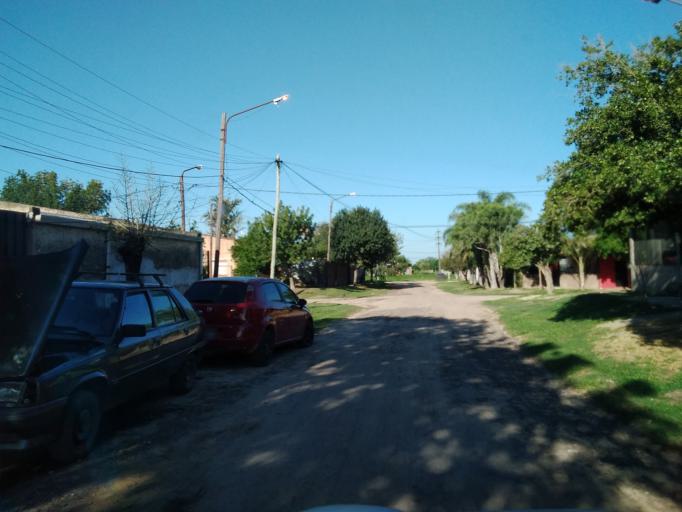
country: AR
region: Corrientes
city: Corrientes
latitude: -27.5035
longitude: -58.7805
